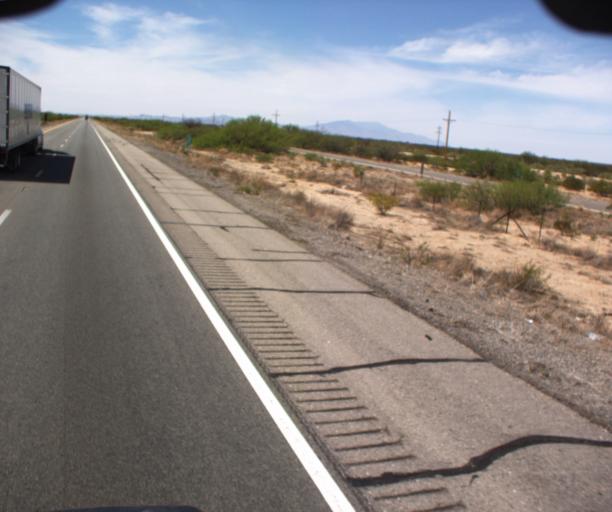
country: US
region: Arizona
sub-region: Cochise County
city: Willcox
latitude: 32.2921
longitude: -109.3301
